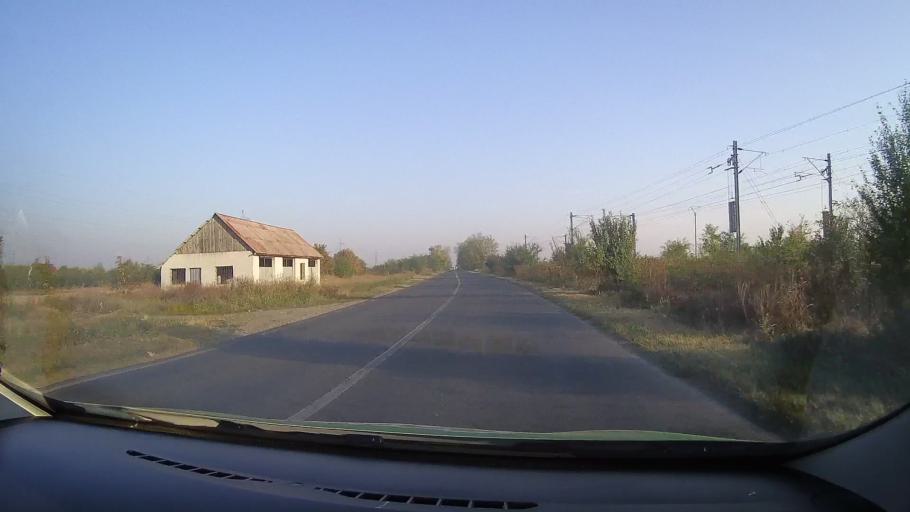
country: RO
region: Arad
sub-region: Comuna Curtici
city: Curtici
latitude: 46.3183
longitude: 21.3070
